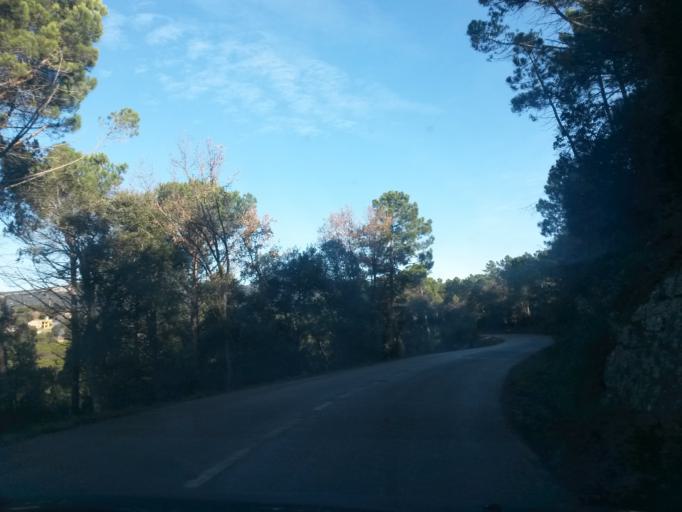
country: ES
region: Catalonia
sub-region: Provincia de Girona
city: la Cellera de Ter
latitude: 42.0084
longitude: 2.6725
